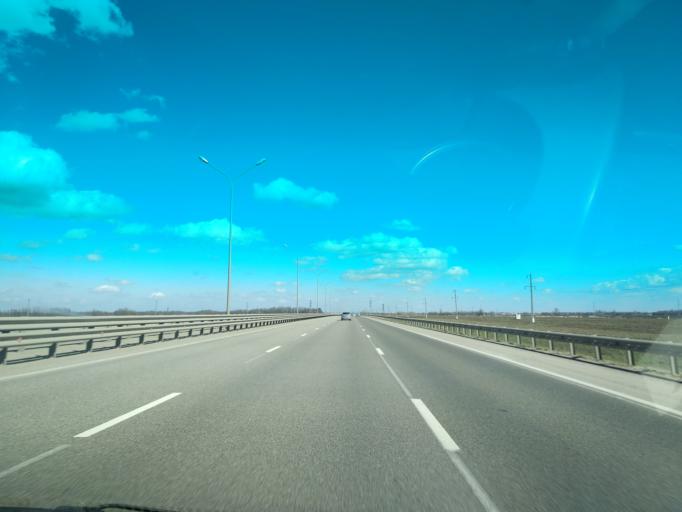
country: RU
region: Krasnodarskiy
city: Dinskaya
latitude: 45.2080
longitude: 39.1573
